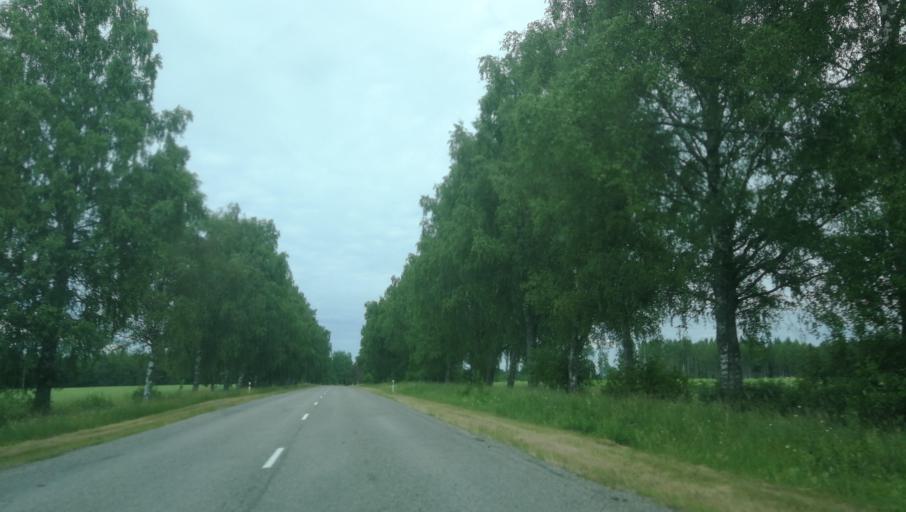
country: LV
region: Valmieras Rajons
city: Valmiera
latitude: 57.6504
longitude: 25.4338
